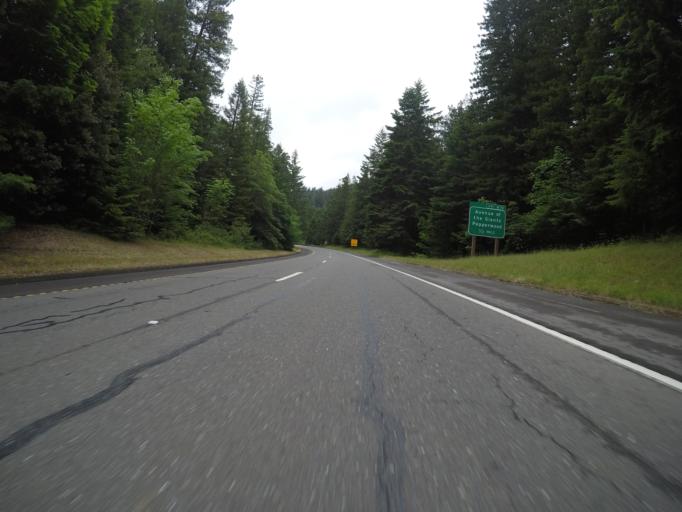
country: US
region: California
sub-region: Humboldt County
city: Rio Dell
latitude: 40.4421
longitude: -124.0391
